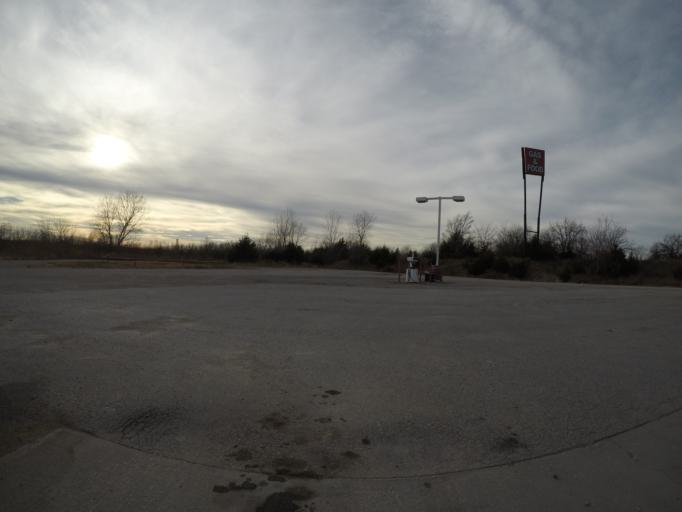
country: US
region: Kansas
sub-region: Osage County
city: Lyndon
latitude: 38.4908
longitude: -95.4756
